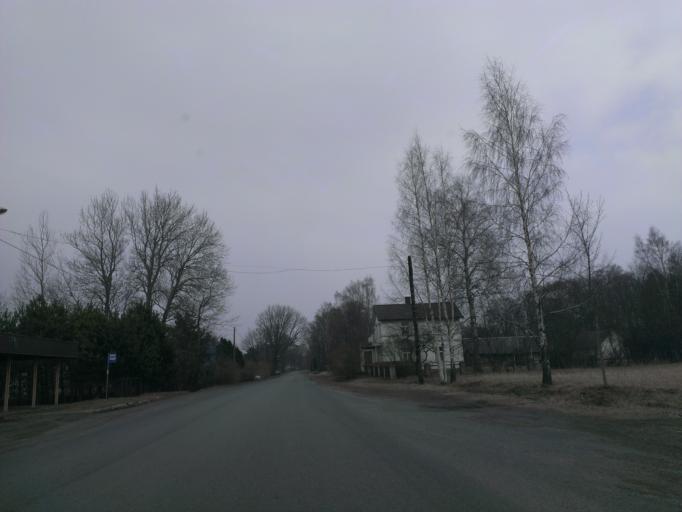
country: LV
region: Salacgrivas
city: Ainazi
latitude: 58.0020
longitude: 24.4382
